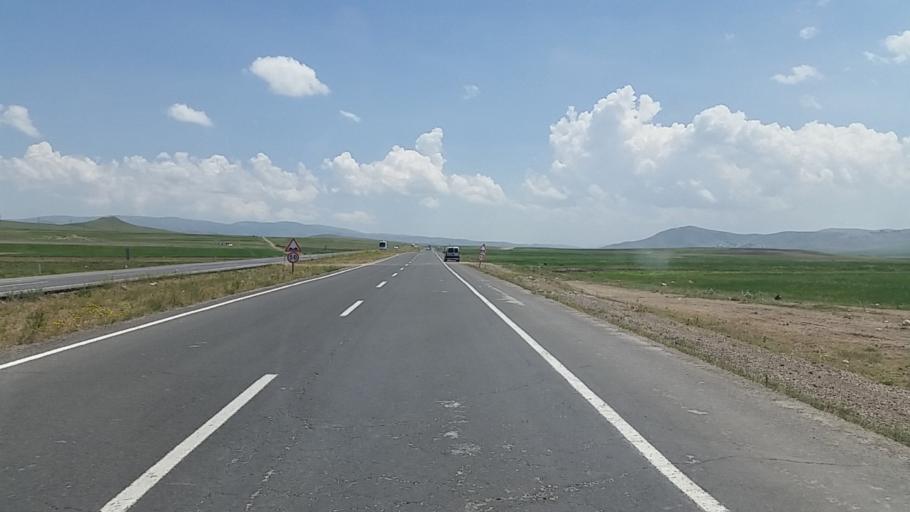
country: TR
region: Agri
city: Taslicay
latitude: 39.6326
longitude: 43.4007
